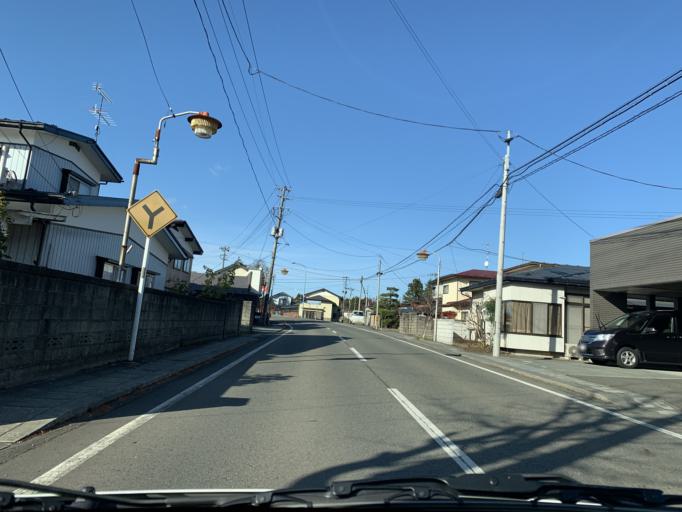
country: JP
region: Iwate
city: Mizusawa
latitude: 39.2010
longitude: 141.1169
